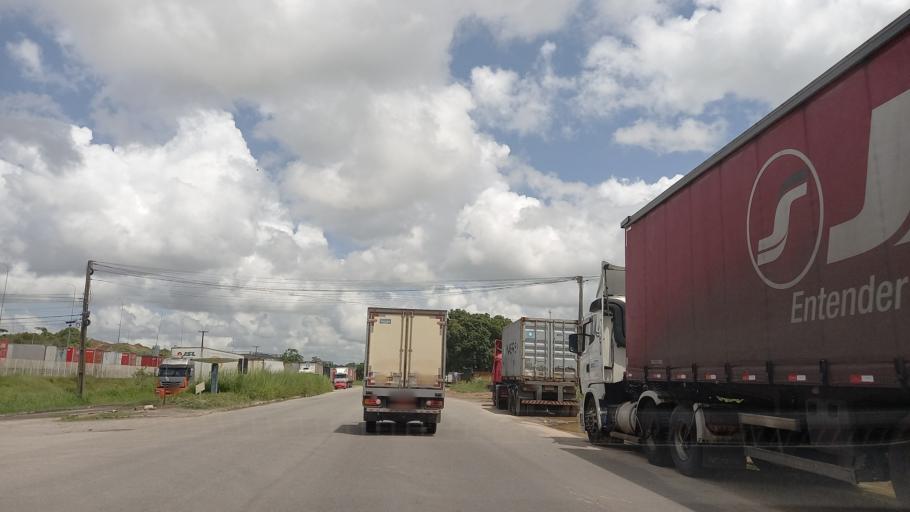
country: BR
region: Pernambuco
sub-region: Cabo De Santo Agostinho
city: Cabo
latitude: -8.2476
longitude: -34.9992
